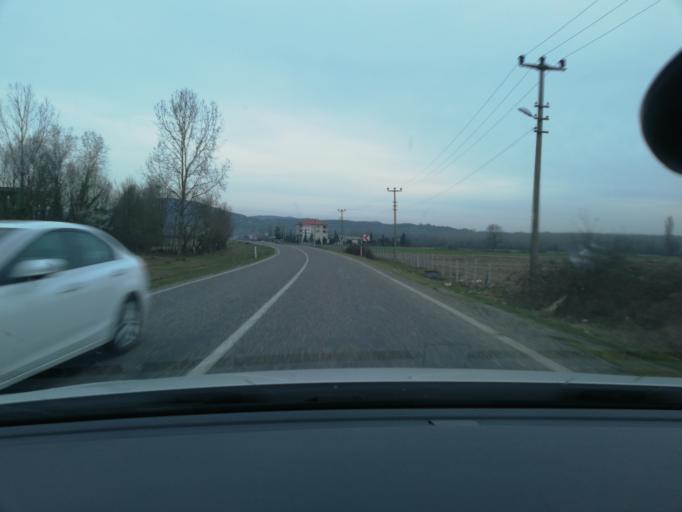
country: TR
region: Zonguldak
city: Saltukova
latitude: 41.5132
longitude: 32.1033
